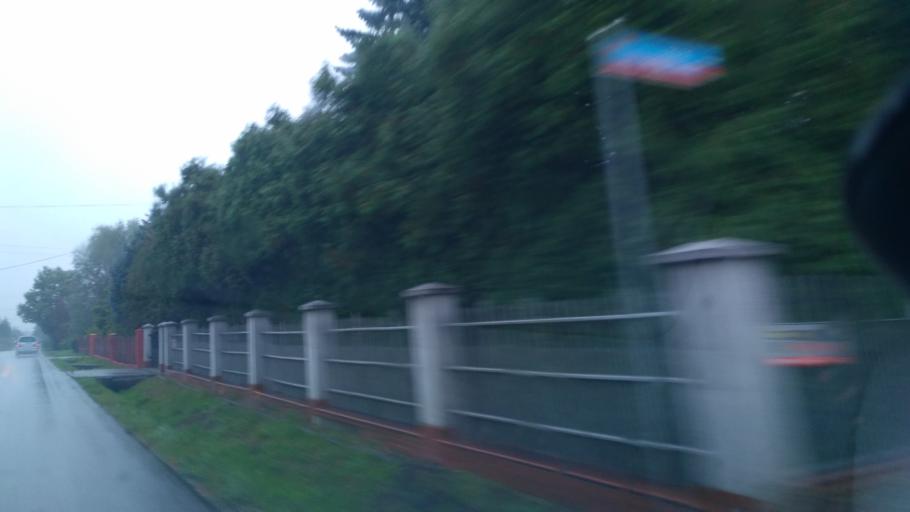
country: PL
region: Subcarpathian Voivodeship
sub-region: Powiat krosnienski
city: Miejsce Piastowe
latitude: 49.6481
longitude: 21.8104
